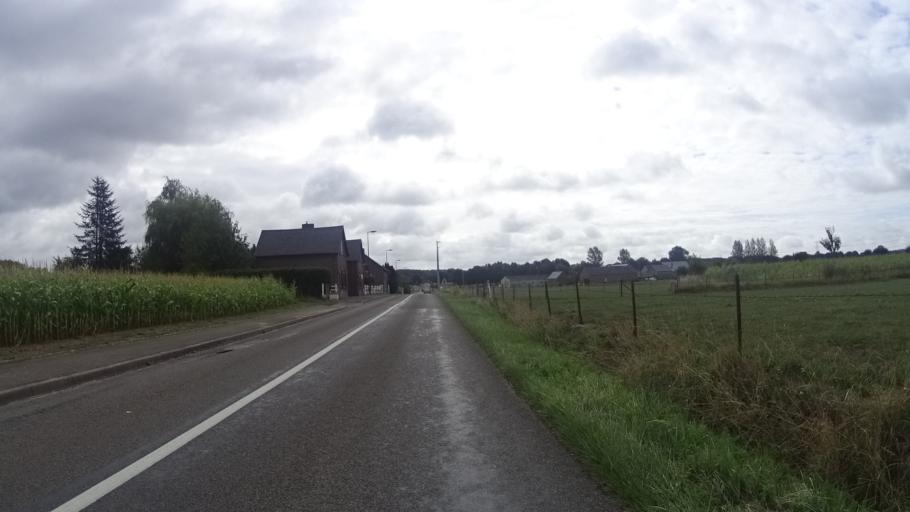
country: FR
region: Picardie
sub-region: Departement de l'Aisne
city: Boue
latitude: 50.0010
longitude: 3.6865
